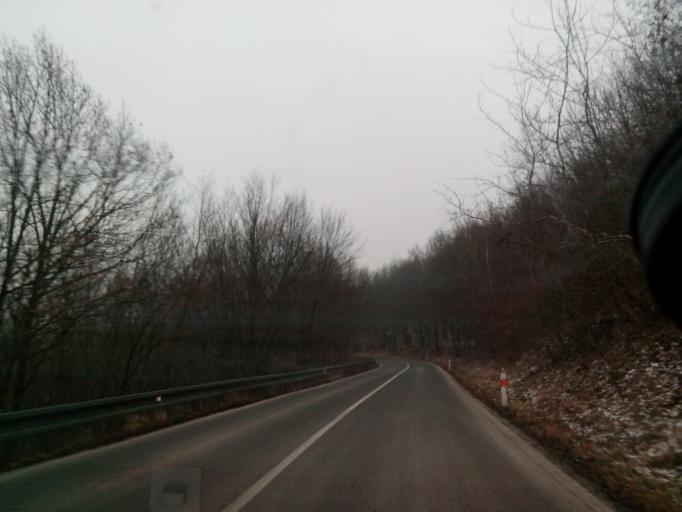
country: SK
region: Kosicky
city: Kosice
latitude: 48.7105
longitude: 21.1985
